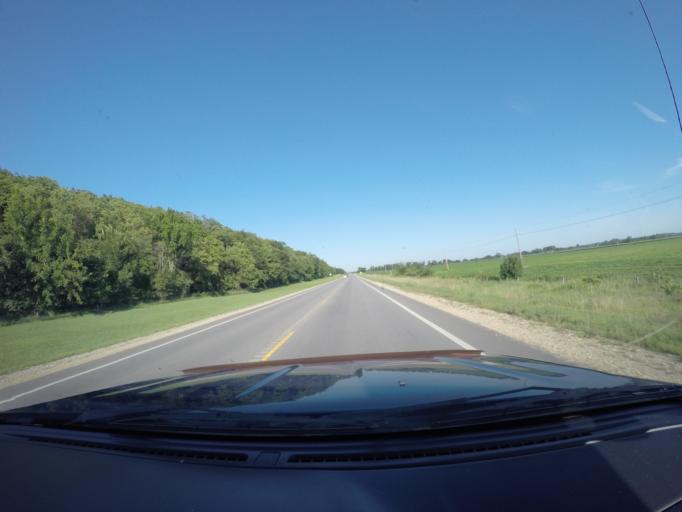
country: US
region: Kansas
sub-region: Jefferson County
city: Oskaloosa
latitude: 39.0773
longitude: -95.3762
